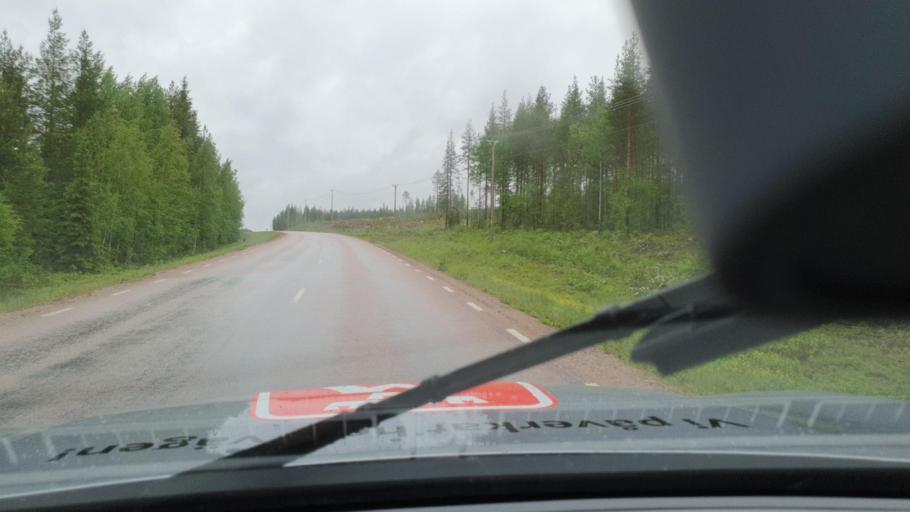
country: SE
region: Norrbotten
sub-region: Overkalix Kommun
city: OEverkalix
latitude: 66.3987
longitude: 22.9521
